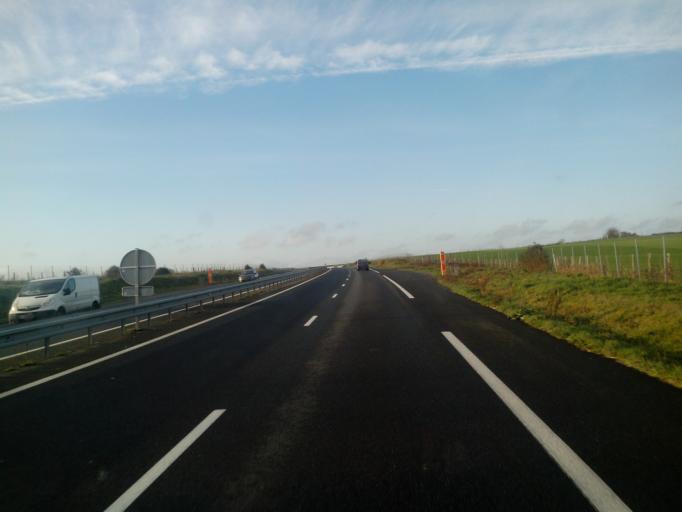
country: FR
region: Poitou-Charentes
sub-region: Departement des Deux-Sevres
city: Combrand
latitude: 46.9149
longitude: -0.6863
